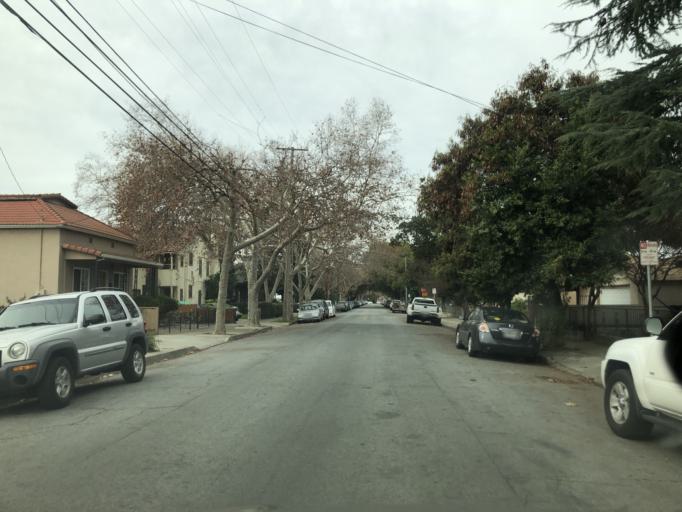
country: US
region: California
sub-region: Santa Clara County
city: San Jose
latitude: 37.3438
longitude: -121.8674
